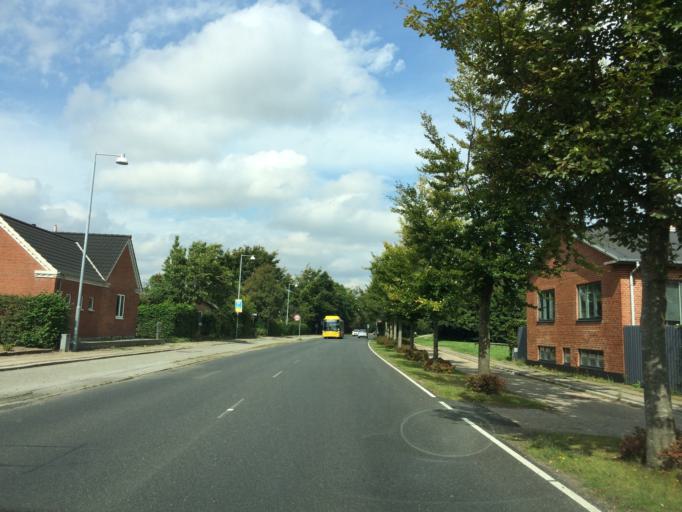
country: DK
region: Central Jutland
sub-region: Holstebro Kommune
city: Holstebro
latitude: 56.3662
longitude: 8.6110
